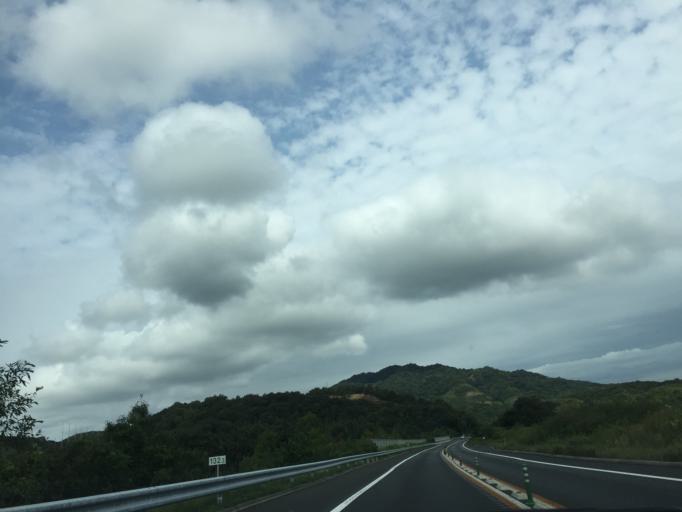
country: JP
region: Kagawa
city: Shido
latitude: 34.2477
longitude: 134.2971
